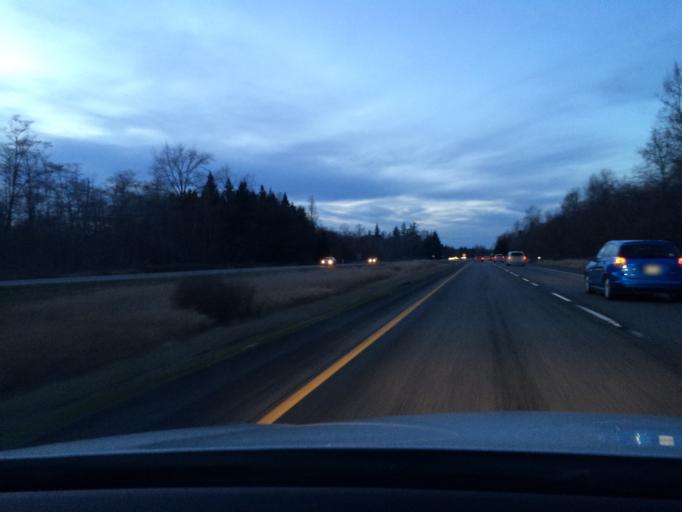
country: US
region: Washington
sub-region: Whatcom County
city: Blaine
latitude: 48.9638
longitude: -122.7058
